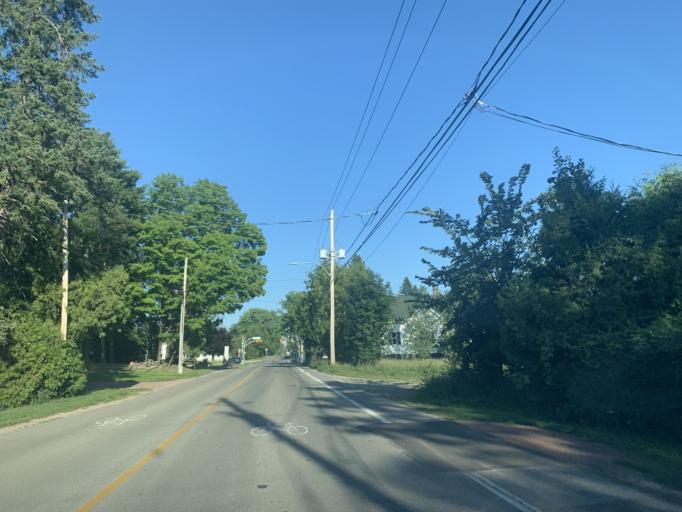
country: CA
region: Ontario
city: Hawkesbury
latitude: 45.6266
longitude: -74.5926
